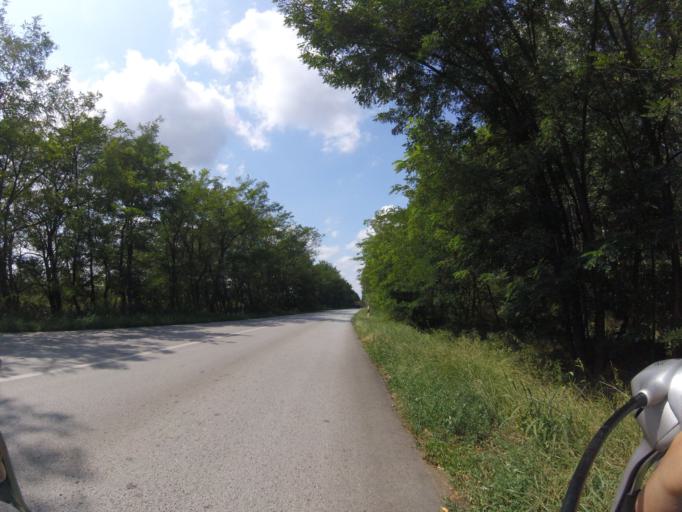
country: HU
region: Szabolcs-Szatmar-Bereg
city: Nyirbogdany
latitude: 48.0589
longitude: 21.8524
